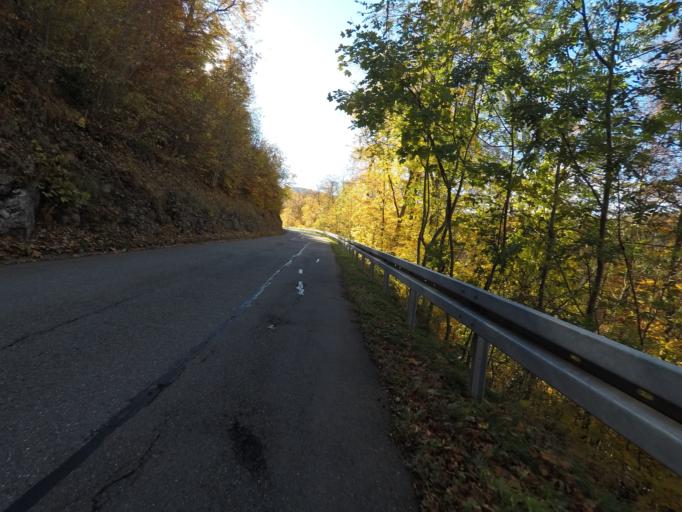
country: DE
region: Baden-Wuerttemberg
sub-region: Tuebingen Region
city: Pfullingen
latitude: 48.4161
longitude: 9.2381
